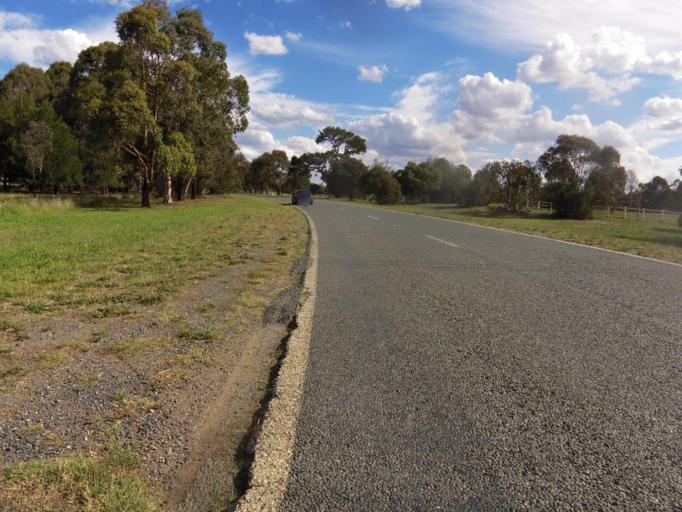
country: AU
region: Australian Capital Territory
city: Belconnen
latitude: -35.1748
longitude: 149.0713
